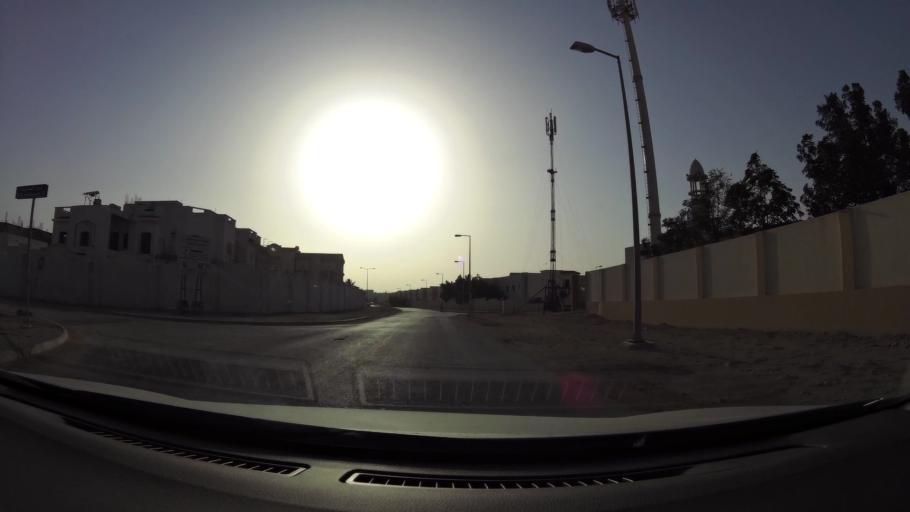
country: QA
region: Baladiyat ar Rayyan
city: Ar Rayyan
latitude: 25.3350
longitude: 51.4516
